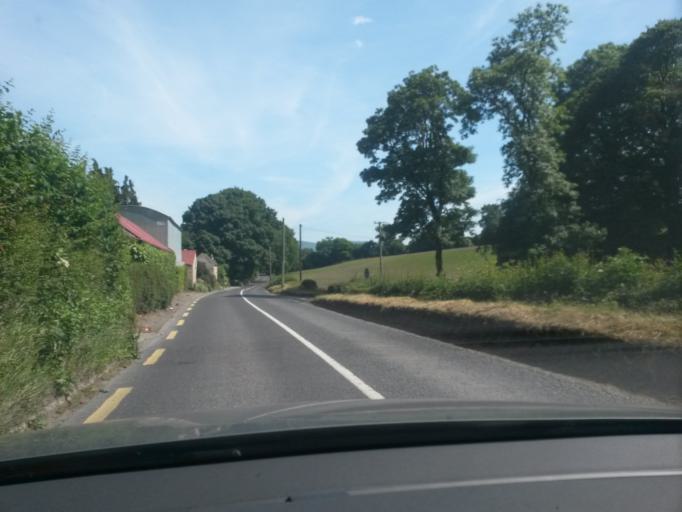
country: IE
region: Leinster
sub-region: Wicklow
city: Blessington
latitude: 53.1775
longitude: -6.5607
